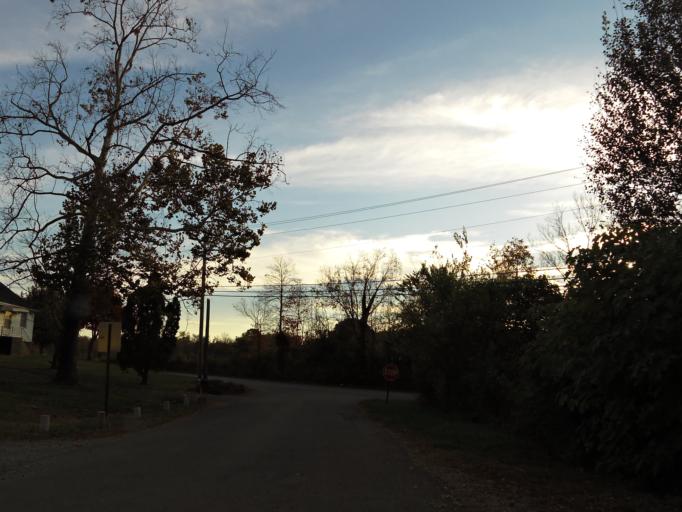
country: US
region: Tennessee
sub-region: Blount County
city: Alcoa
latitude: 35.7861
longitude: -83.9550
